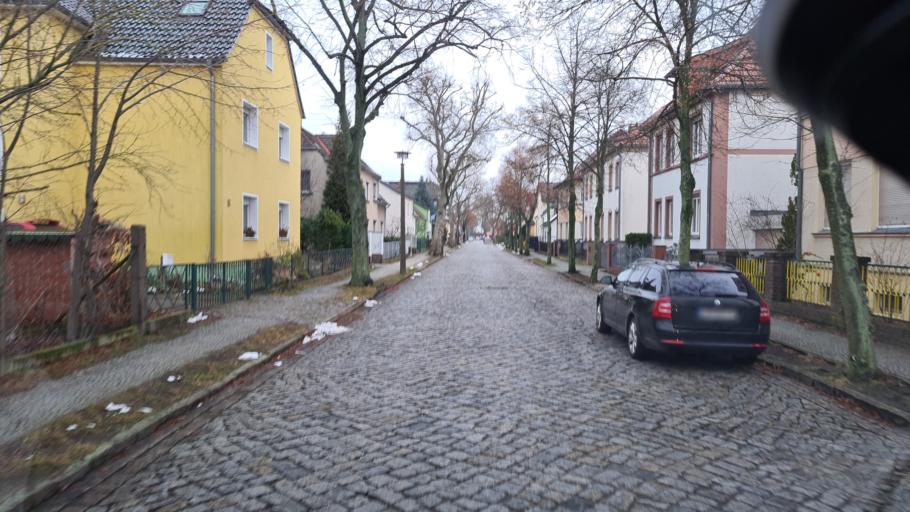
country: DE
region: Brandenburg
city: Eisenhuettenstadt
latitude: 52.1457
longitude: 14.6592
